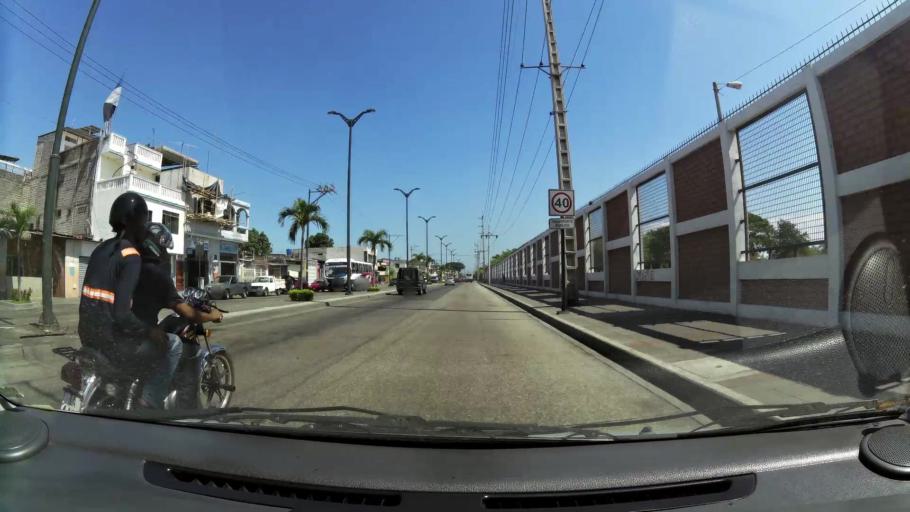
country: EC
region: Guayas
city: Guayaquil
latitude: -2.2172
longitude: -79.9370
